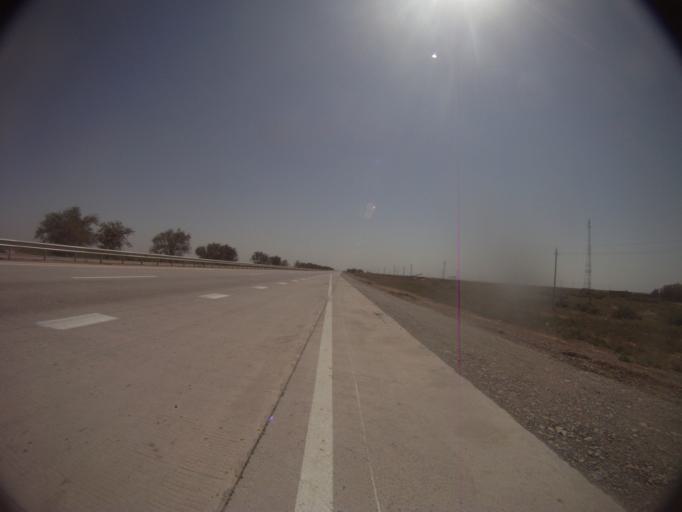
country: KZ
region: Ongtustik Qazaqstan
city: Bayaldyr
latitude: 43.0596
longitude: 68.6851
